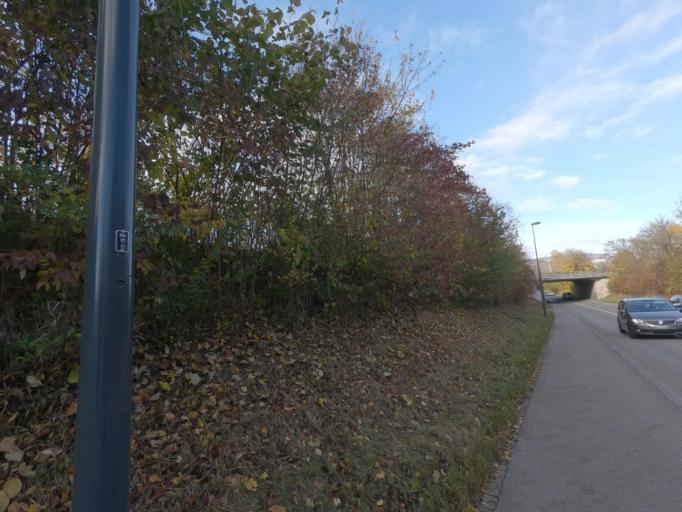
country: CH
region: Solothurn
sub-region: Bezirk Wasseramt
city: Luterbach
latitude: 47.2088
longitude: 7.5855
